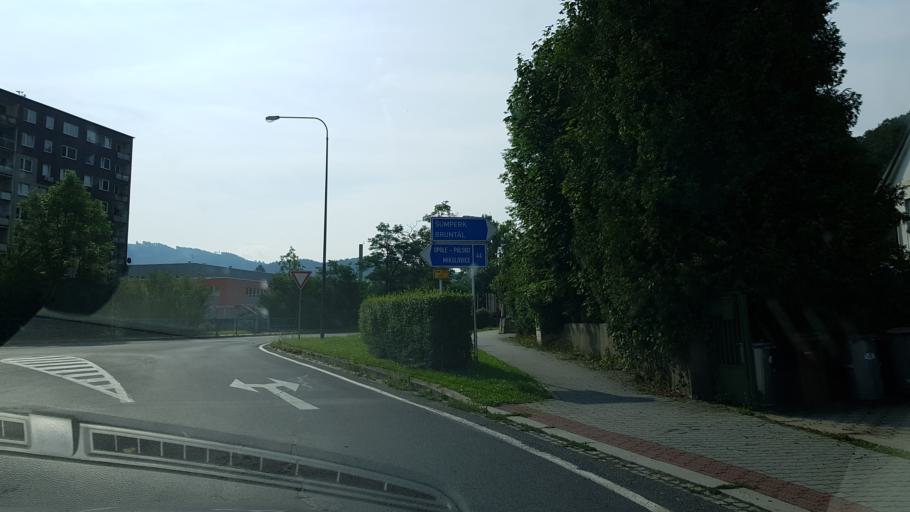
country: CZ
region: Olomoucky
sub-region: Okres Jesenik
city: Jesenik
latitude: 50.2239
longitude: 17.2074
